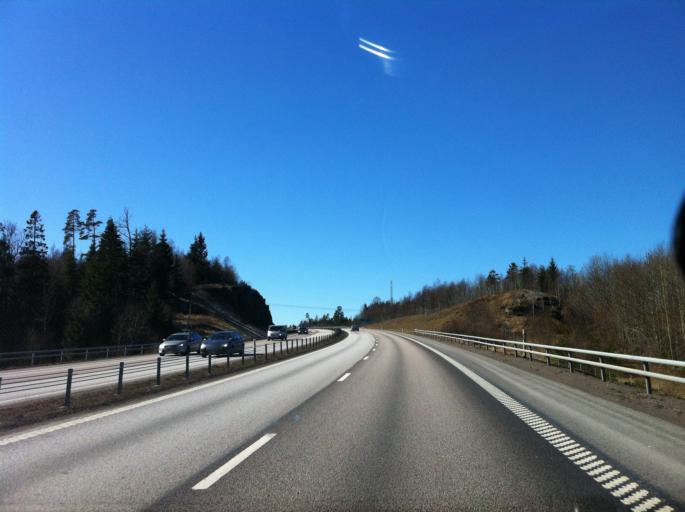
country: SE
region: Vaestra Goetaland
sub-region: Vanersborgs Kommun
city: Vanersborg
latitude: 58.3752
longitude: 12.3412
